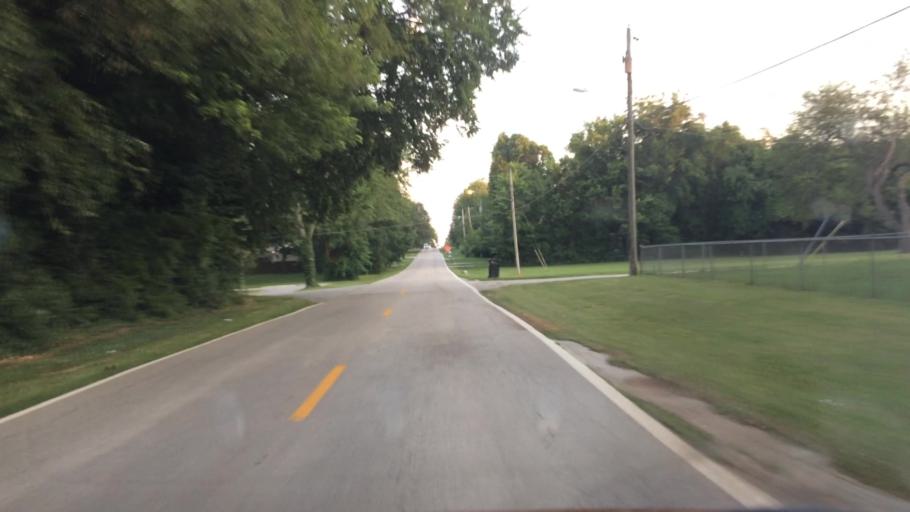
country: US
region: Missouri
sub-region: Greene County
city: Springfield
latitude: 37.2110
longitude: -93.3740
